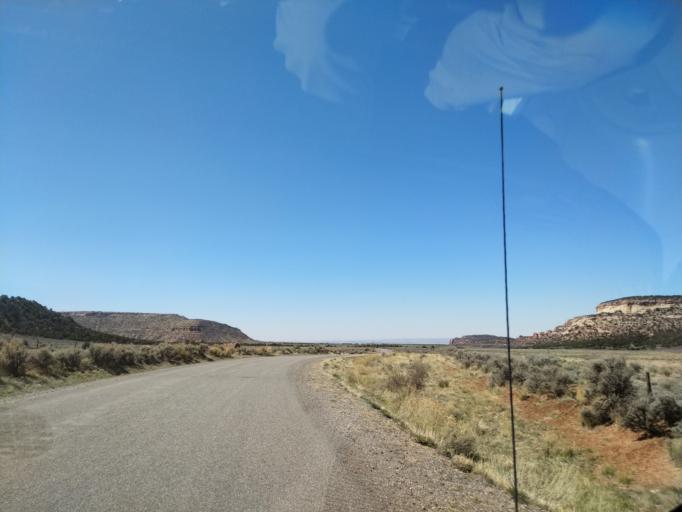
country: US
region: Colorado
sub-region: Mesa County
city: Loma
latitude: 38.9589
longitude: -109.0135
